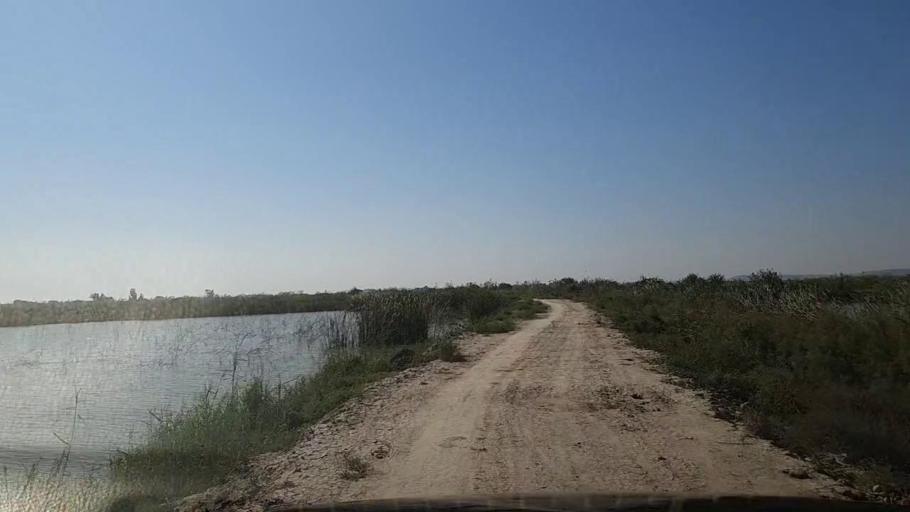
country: PK
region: Sindh
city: Thatta
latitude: 24.6745
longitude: 67.8888
